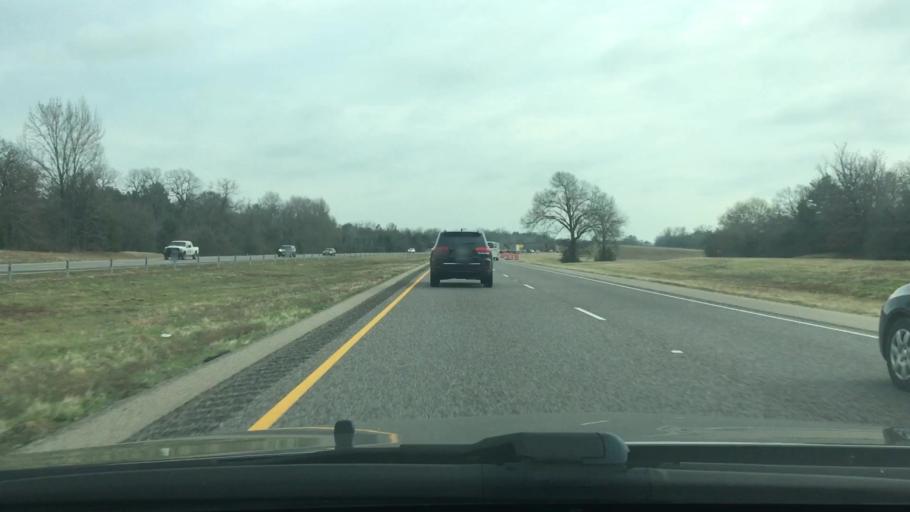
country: US
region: Texas
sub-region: Leon County
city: Buffalo
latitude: 31.5052
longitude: -96.0997
